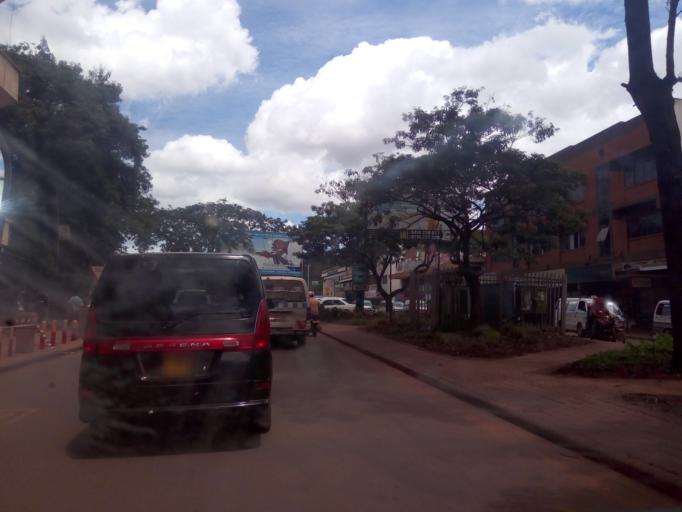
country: UG
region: Central Region
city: Kampala Central Division
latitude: 0.3192
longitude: 32.5743
